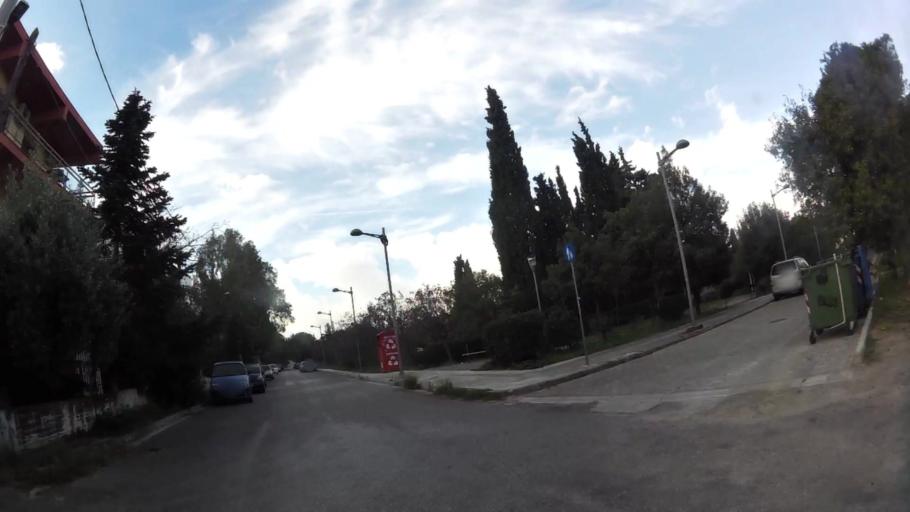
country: GR
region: Attica
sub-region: Nomarchia Athinas
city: Vrilissia
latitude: 38.0377
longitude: 23.8218
